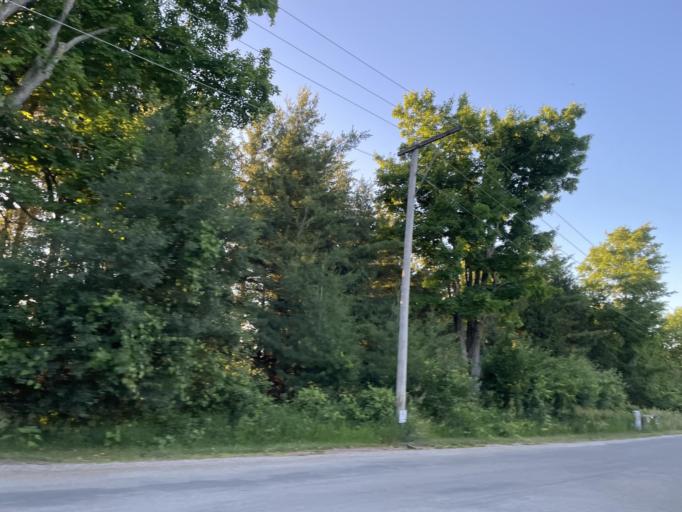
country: CA
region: Ontario
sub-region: Wellington County
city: Guelph
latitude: 43.6061
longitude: -80.2563
